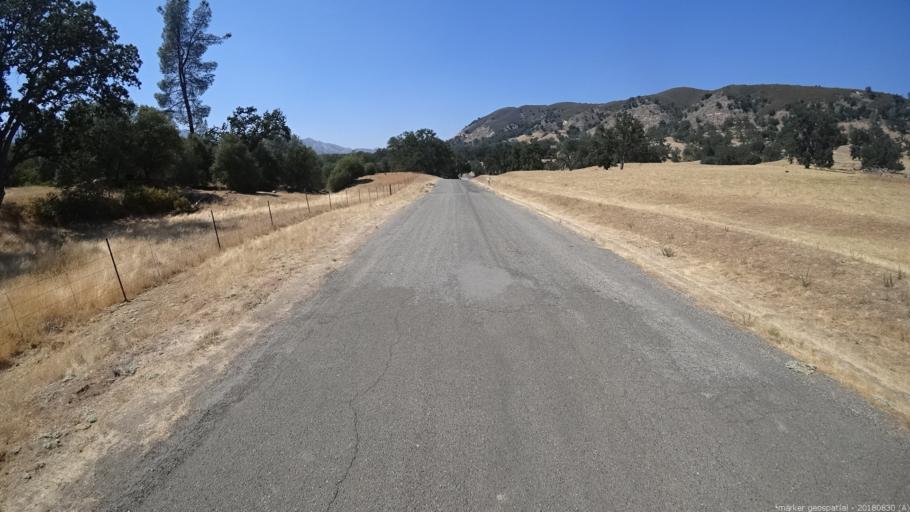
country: US
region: California
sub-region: Monterey County
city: Greenfield
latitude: 36.0854
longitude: -121.4026
